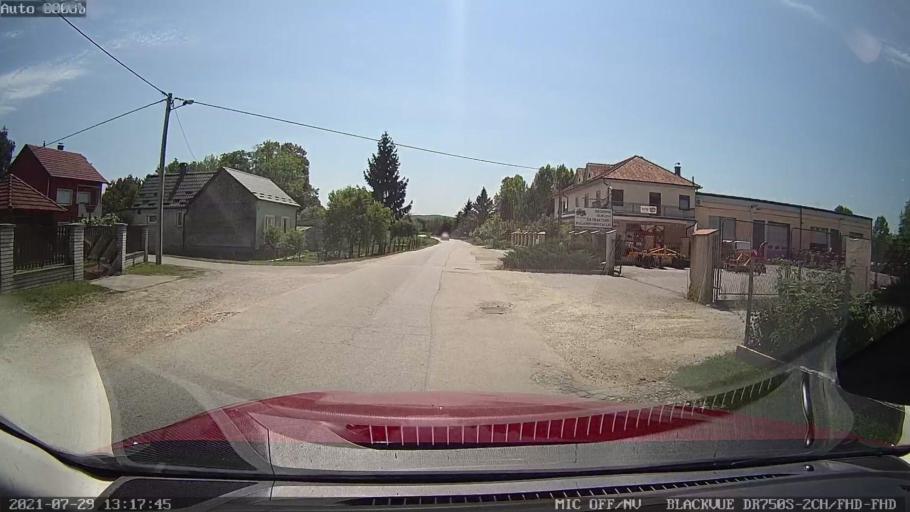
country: HR
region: Varazdinska
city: Varazdin
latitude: 46.2754
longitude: 16.3827
